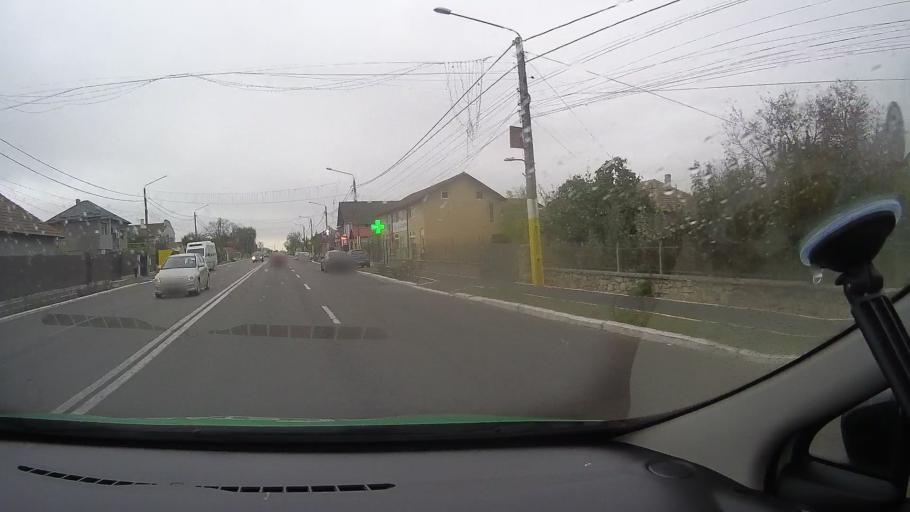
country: RO
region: Constanta
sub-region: Comuna Valu lui Traian
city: Valu lui Traian
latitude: 44.1647
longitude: 28.4777
